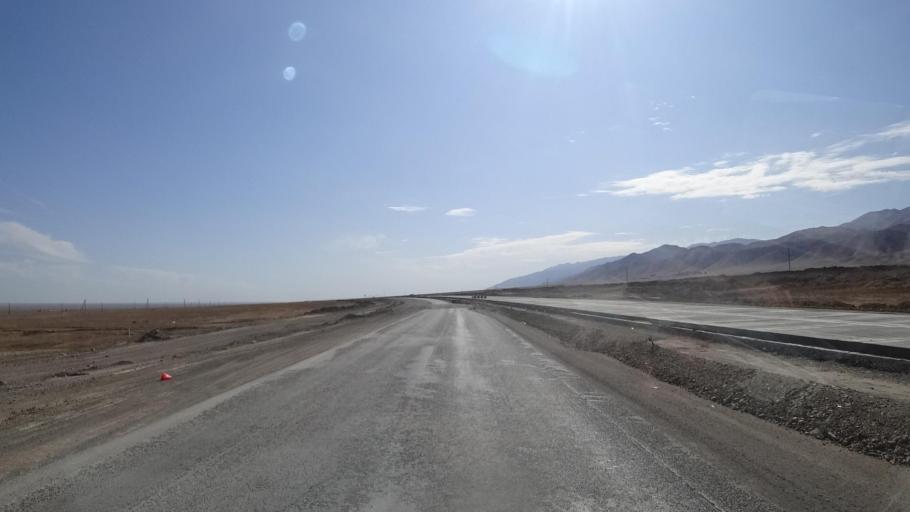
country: KG
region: Chuy
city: Ivanovka
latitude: 43.3877
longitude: 75.1496
